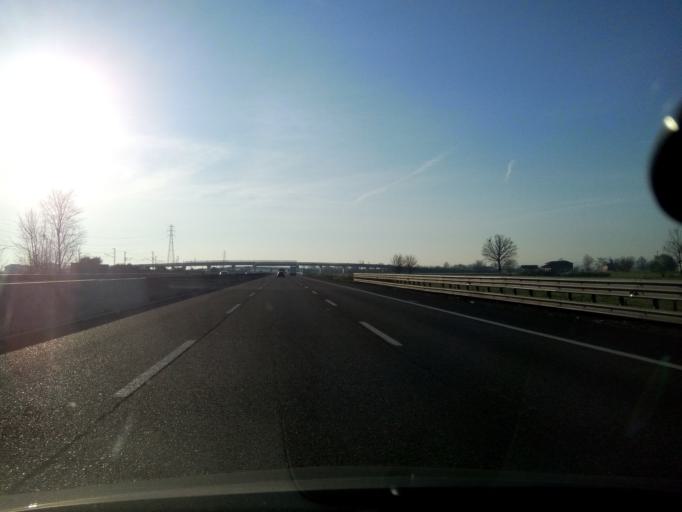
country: IT
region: Emilia-Romagna
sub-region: Provincia di Piacenza
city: Fiorenzuola d'Arda
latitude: 44.9472
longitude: 9.9416
